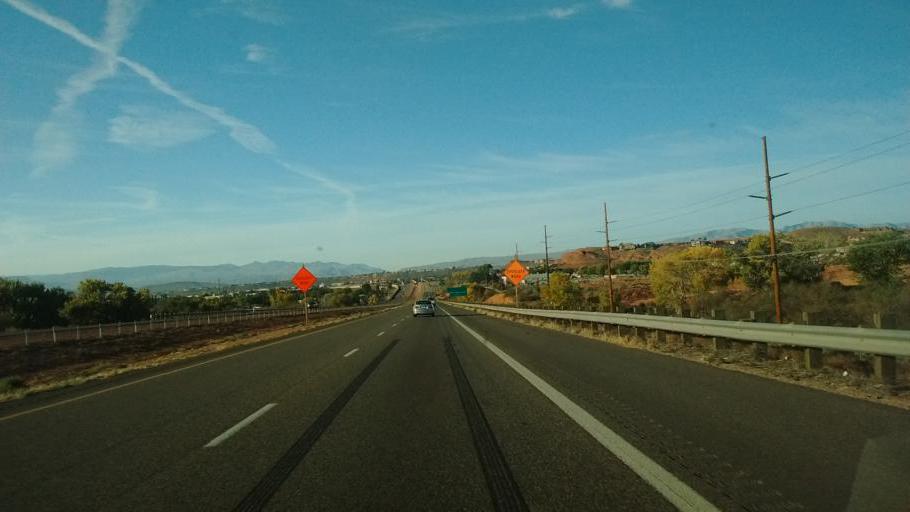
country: US
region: Utah
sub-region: Washington County
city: Washington
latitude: 37.1376
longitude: -113.5120
